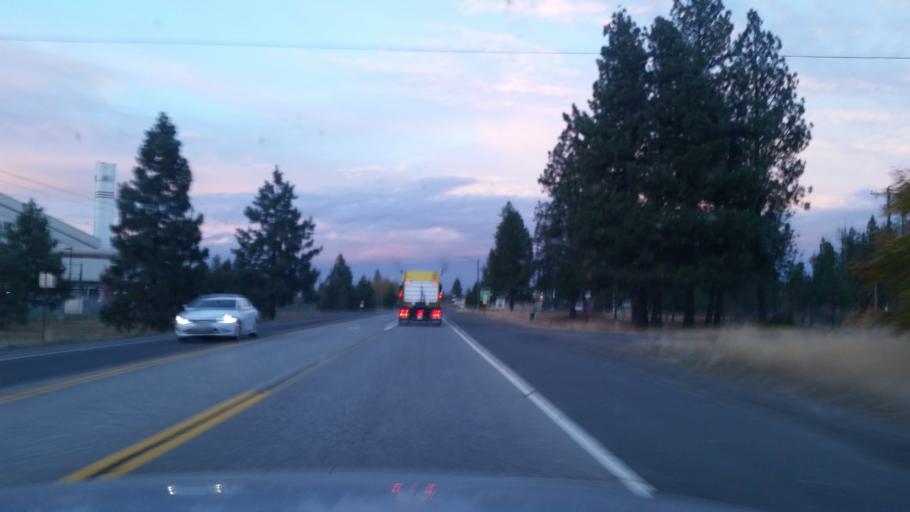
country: US
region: Washington
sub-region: Spokane County
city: Spokane
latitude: 47.6239
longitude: -117.5043
